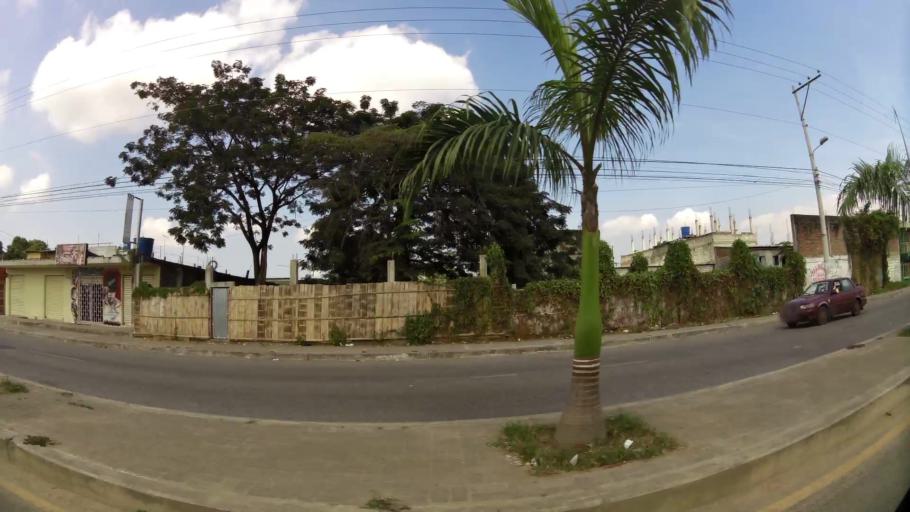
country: EC
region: Guayas
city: Eloy Alfaro
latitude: -2.1648
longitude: -79.8350
